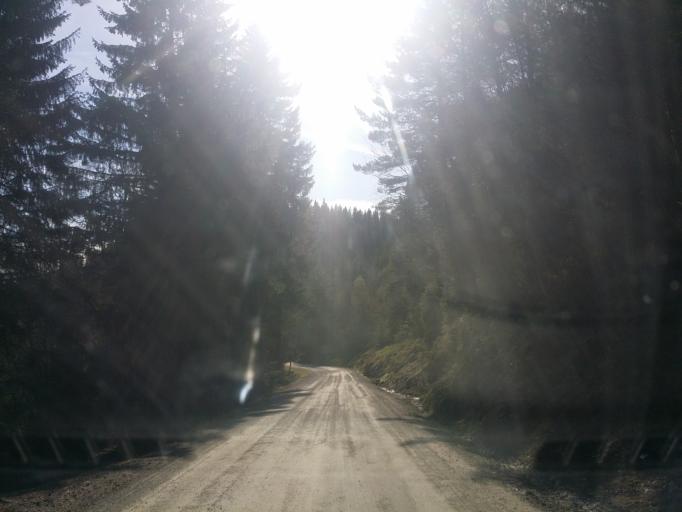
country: NO
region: Telemark
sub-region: Seljord
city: Seljord
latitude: 59.6174
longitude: 8.6892
